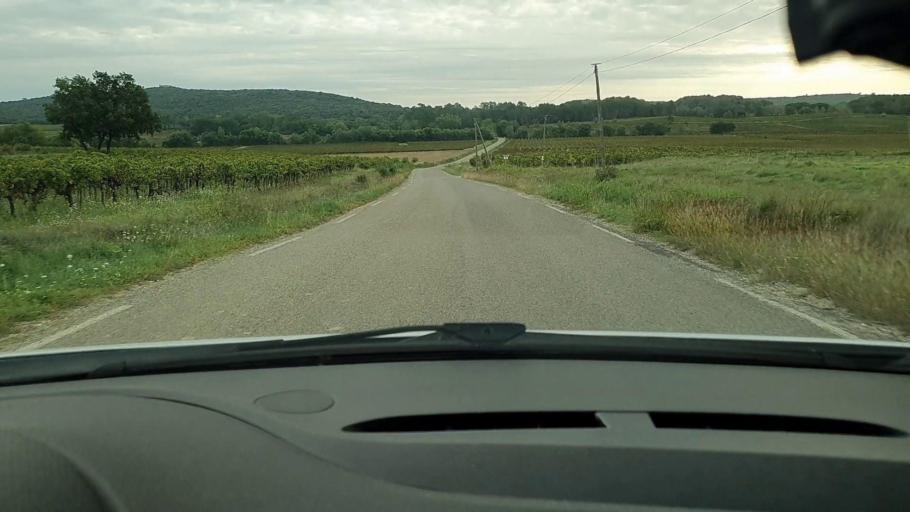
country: FR
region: Languedoc-Roussillon
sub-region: Departement du Gard
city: Moussac
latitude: 44.0336
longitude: 4.2488
